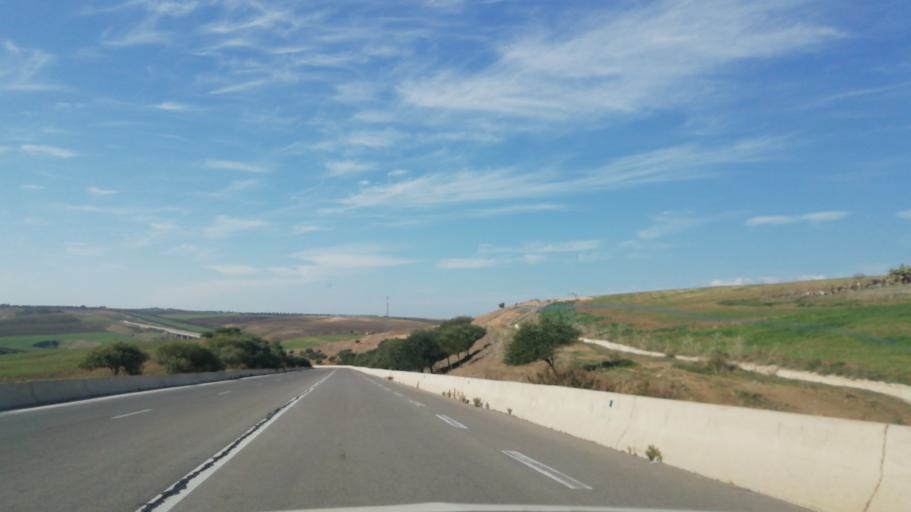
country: DZ
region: Tlemcen
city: Chetouane
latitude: 34.9815
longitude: -1.2253
